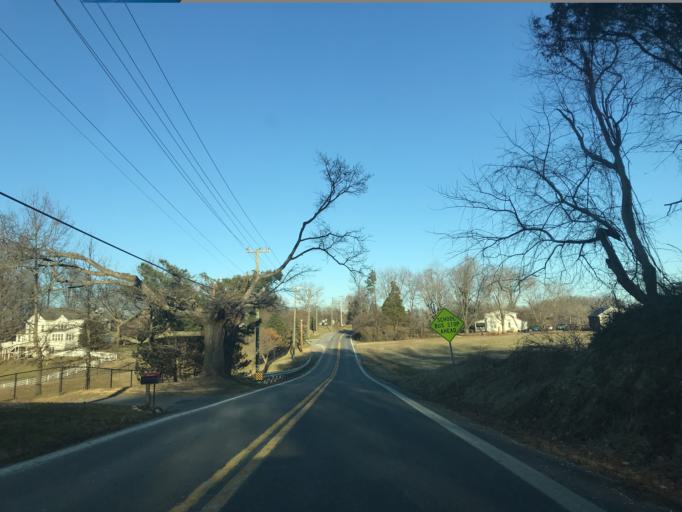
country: US
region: Maryland
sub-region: Prince George's County
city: Marlboro Meadows
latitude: 38.8390
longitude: -76.6411
